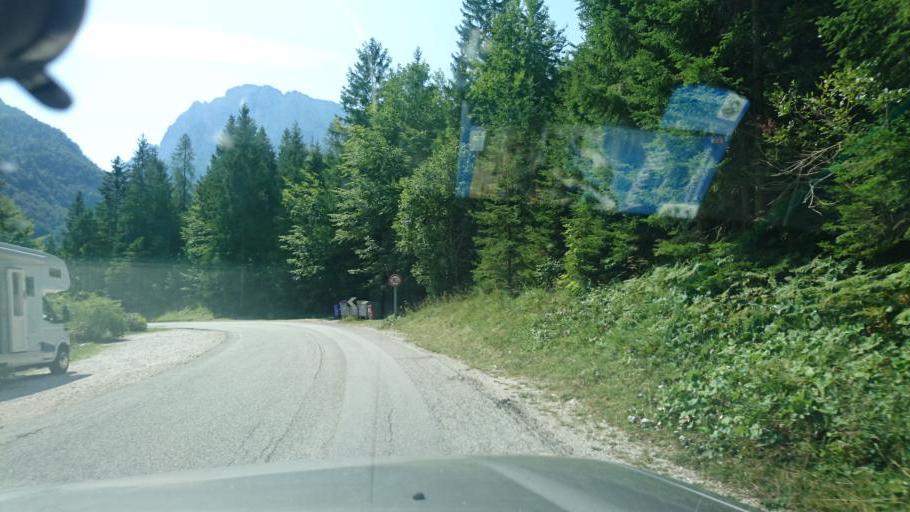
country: IT
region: Friuli Venezia Giulia
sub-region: Provincia di Udine
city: Tarvisio
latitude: 46.4262
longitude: 13.5652
